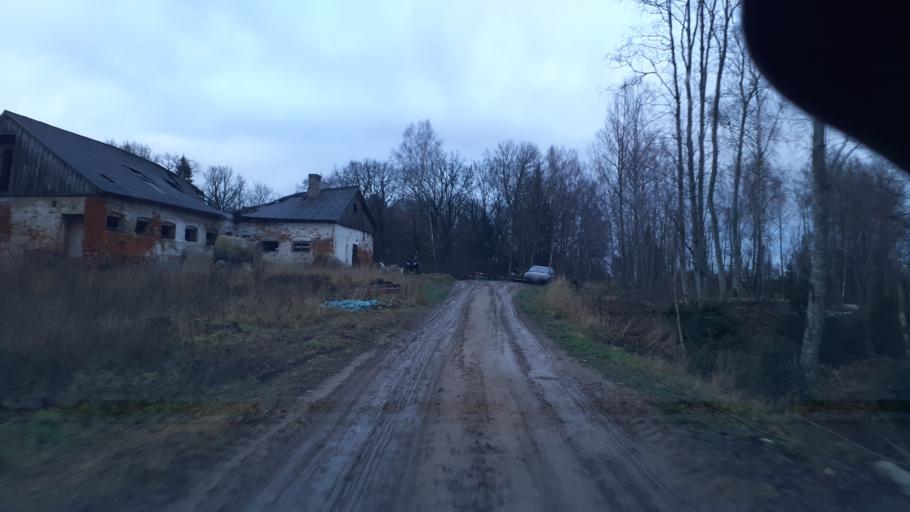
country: LV
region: Alsunga
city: Alsunga
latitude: 56.9072
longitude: 21.6967
